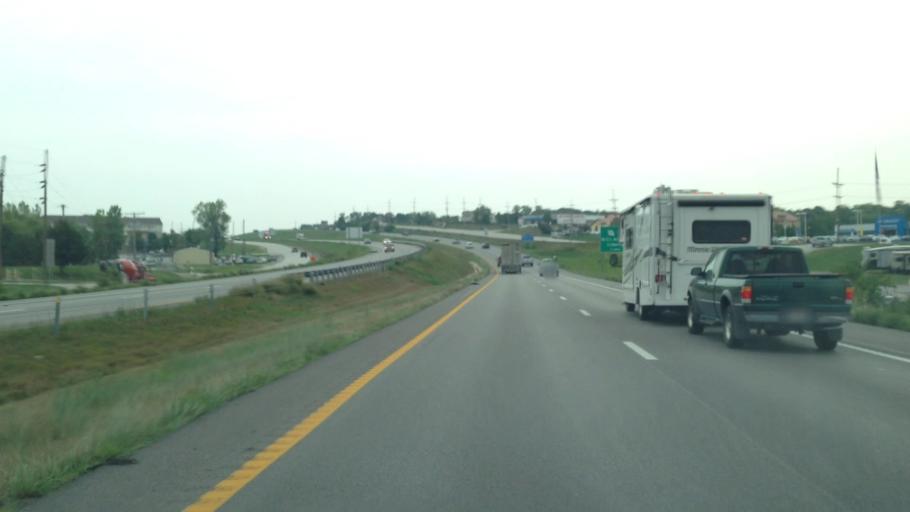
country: US
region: Missouri
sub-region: Clay County
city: Liberty
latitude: 39.2510
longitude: -94.4515
